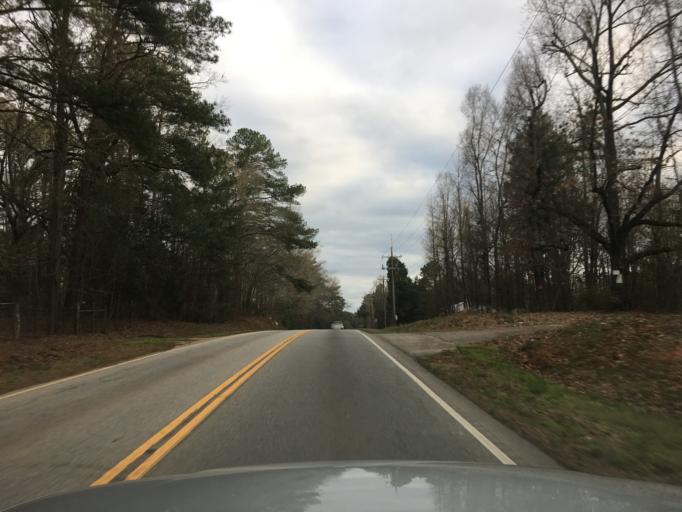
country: US
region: South Carolina
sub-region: Saluda County
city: Saluda
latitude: 33.9930
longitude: -81.7712
